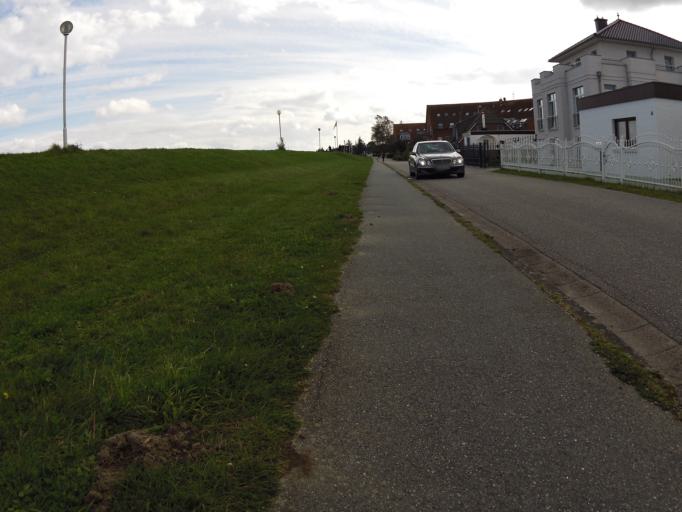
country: DE
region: Schleswig-Holstein
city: Wisch
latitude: 54.4292
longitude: 10.3644
